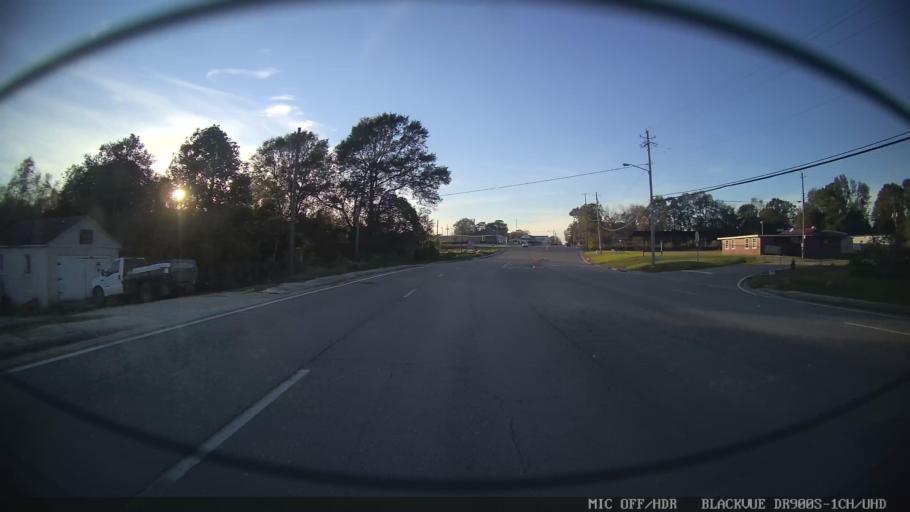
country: US
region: Mississippi
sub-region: Lamar County
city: Lumberton
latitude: 30.9993
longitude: -89.4463
